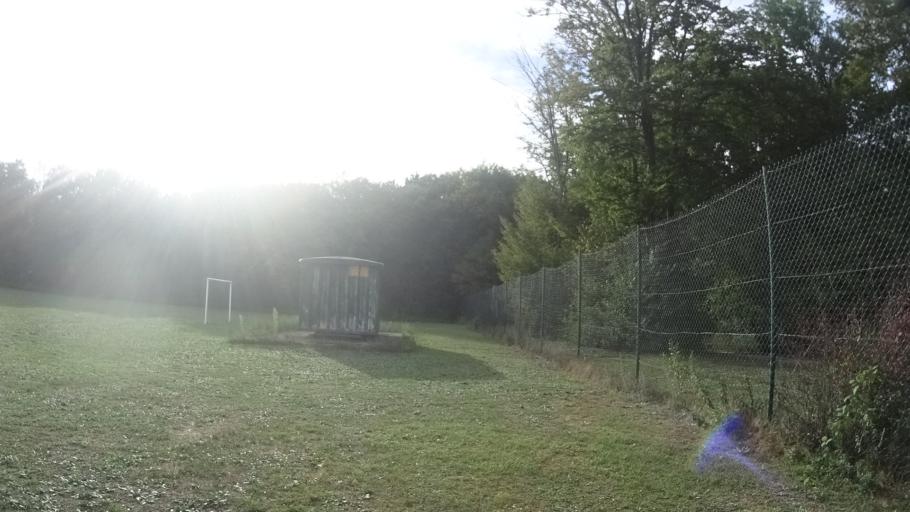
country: FR
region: Picardie
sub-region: Departement de l'Oise
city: Ver-sur-Launette
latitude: 49.1723
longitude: 2.6758
